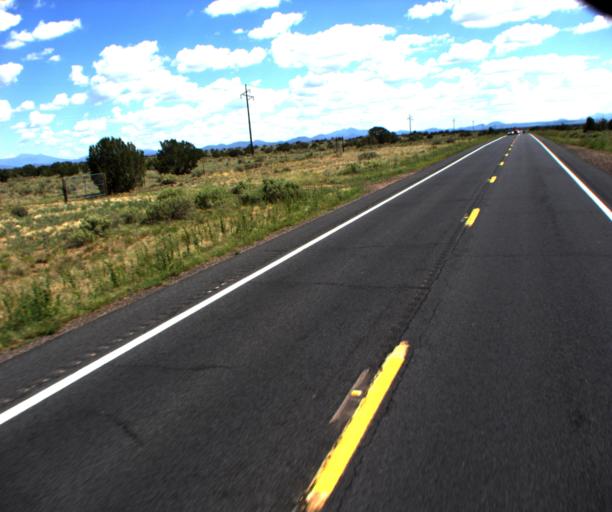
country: US
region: Arizona
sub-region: Coconino County
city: Grand Canyon Village
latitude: 35.7249
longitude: -112.1312
